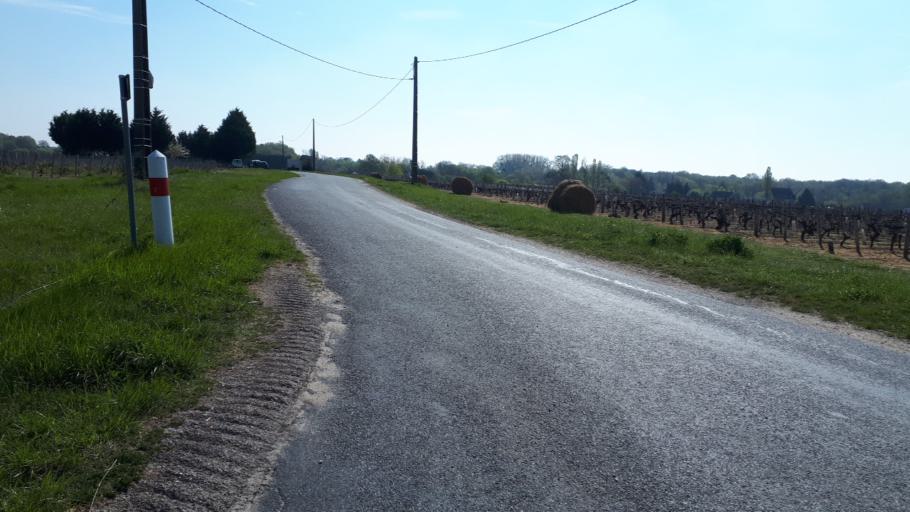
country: FR
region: Centre
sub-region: Departement du Loir-et-Cher
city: Saint-Romain-sur-Cher
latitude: 47.3660
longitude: 1.3906
